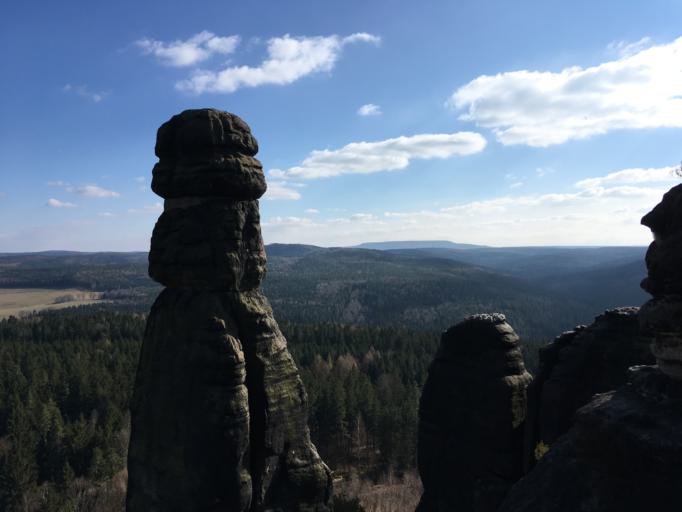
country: DE
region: Saxony
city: Konigstein
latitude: 50.8970
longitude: 14.0813
